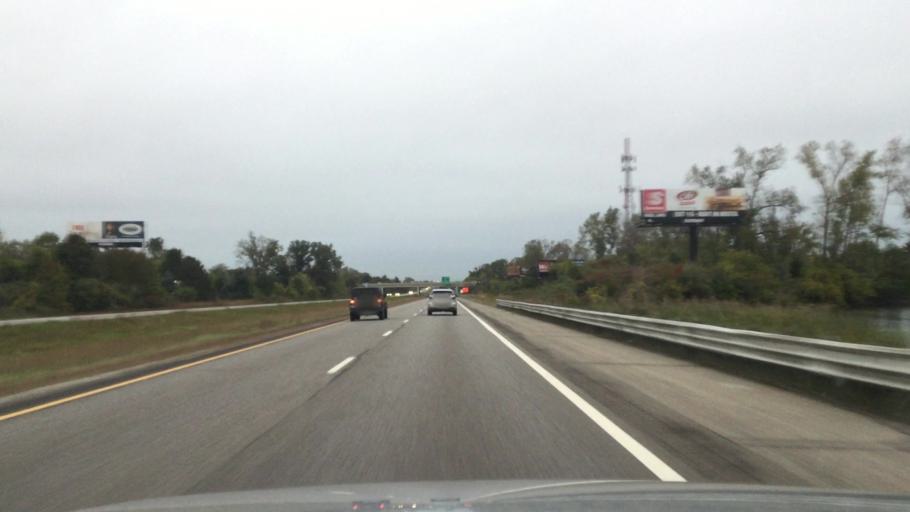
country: US
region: Michigan
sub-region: Genesee County
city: Flint
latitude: 42.9408
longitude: -83.7084
